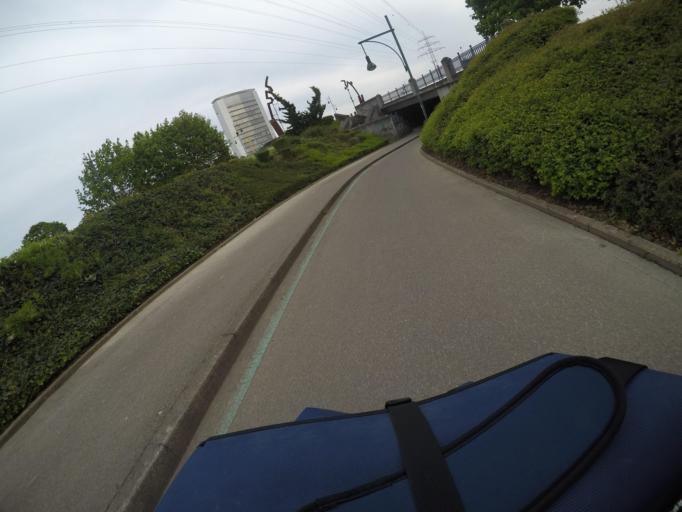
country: DE
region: Baden-Wuerttemberg
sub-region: Freiburg Region
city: Offenburg
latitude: 48.4675
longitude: 7.9343
